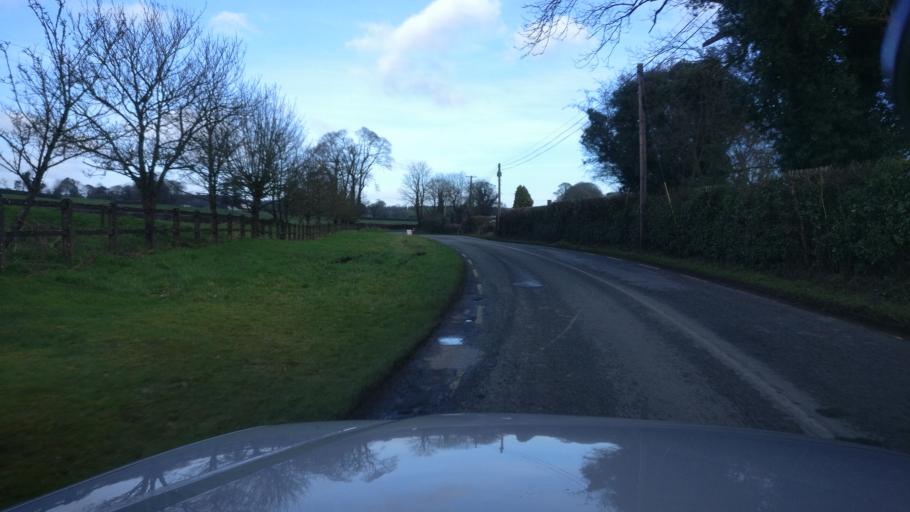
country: IE
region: Leinster
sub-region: Kilkenny
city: Castlecomer
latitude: 52.8222
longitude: -7.2113
